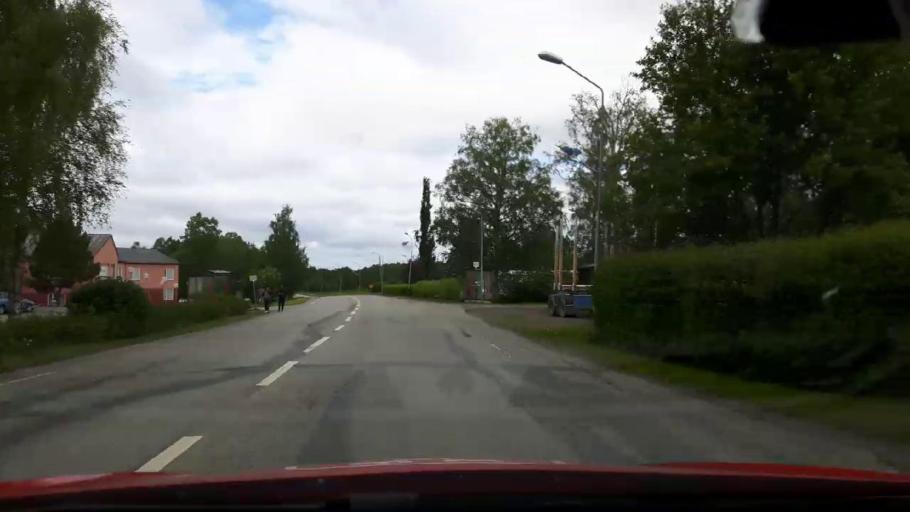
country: SE
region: Jaemtland
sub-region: Krokoms Kommun
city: Krokom
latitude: 63.3041
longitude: 14.4704
